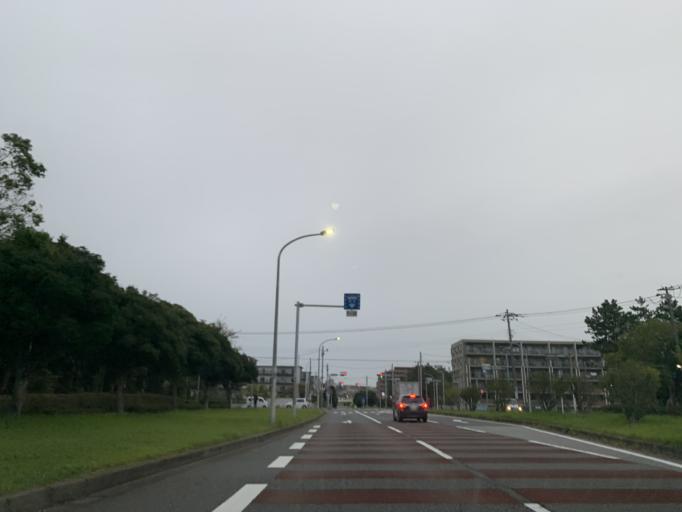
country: JP
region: Chiba
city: Funabashi
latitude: 35.6627
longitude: 140.0352
